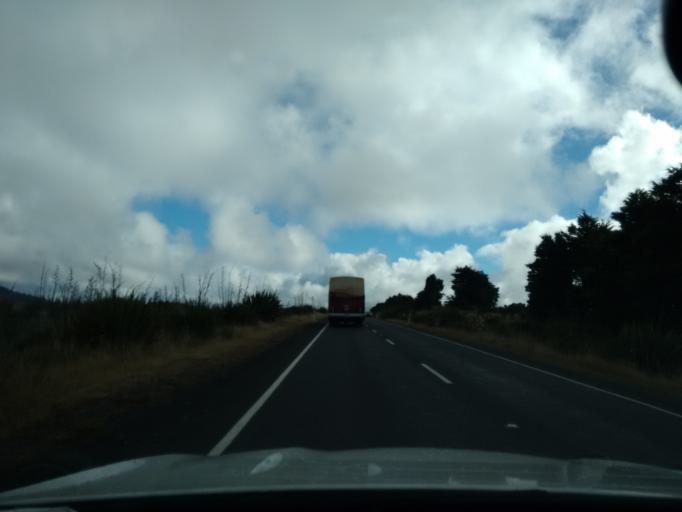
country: NZ
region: Manawatu-Wanganui
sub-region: Ruapehu District
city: Waiouru
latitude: -39.1828
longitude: 175.4410
